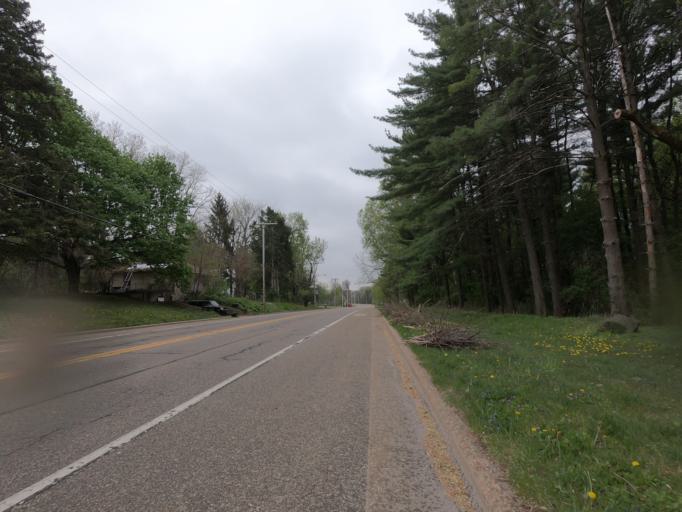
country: US
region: Wisconsin
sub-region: Jefferson County
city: Jefferson
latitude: 43.0206
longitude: -88.8105
